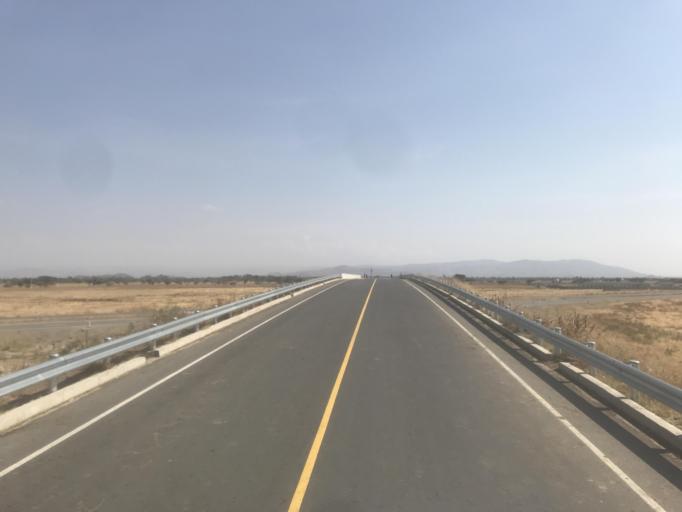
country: ET
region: Oromiya
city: Ziway
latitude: 7.9592
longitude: 38.6933
